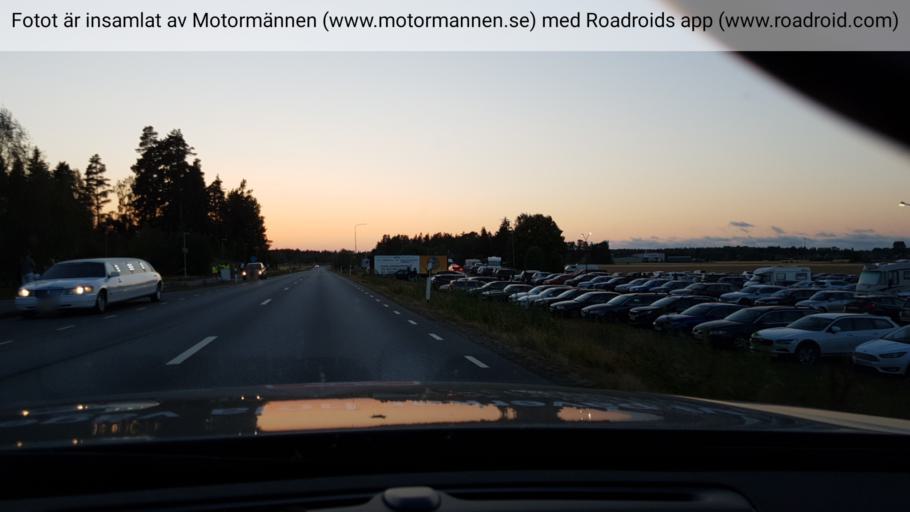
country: SE
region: Uppsala
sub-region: Heby Kommun
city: OEstervala
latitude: 60.1693
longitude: 17.1881
